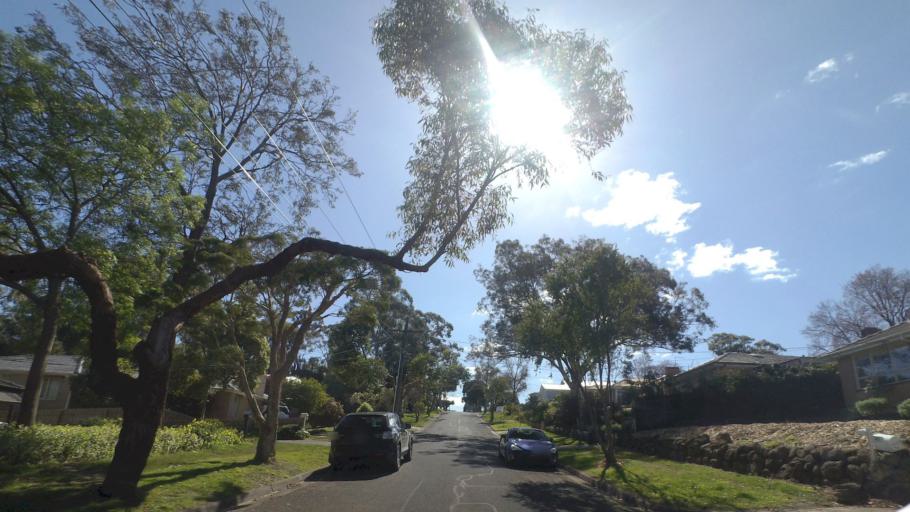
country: AU
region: Victoria
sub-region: Maroondah
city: Heathmont
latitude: -37.8366
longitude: 145.2416
